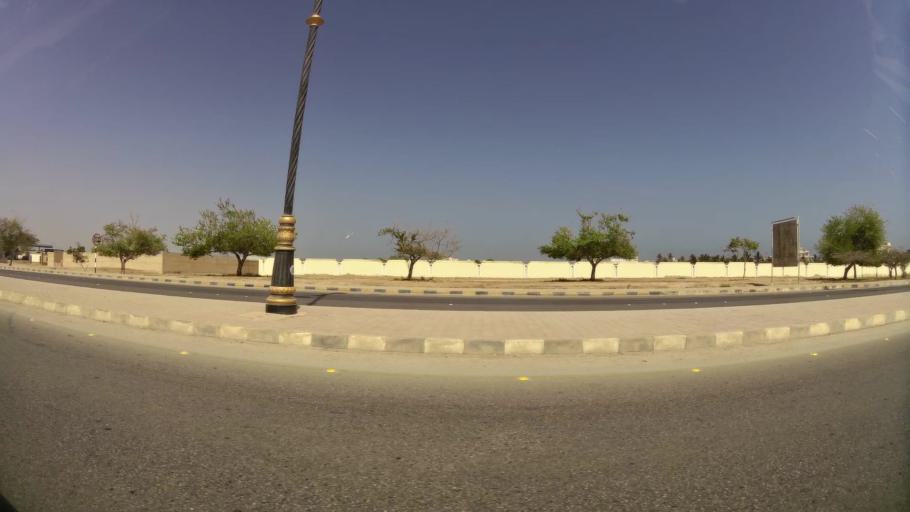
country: OM
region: Zufar
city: Salalah
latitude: 17.0070
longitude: 54.0418
